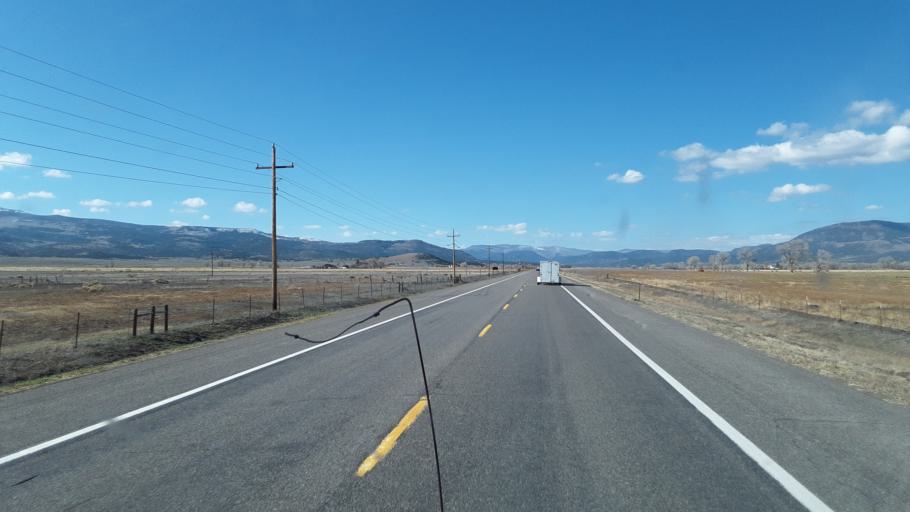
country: US
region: Colorado
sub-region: Rio Grande County
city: Del Norte
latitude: 37.6768
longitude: -106.4355
